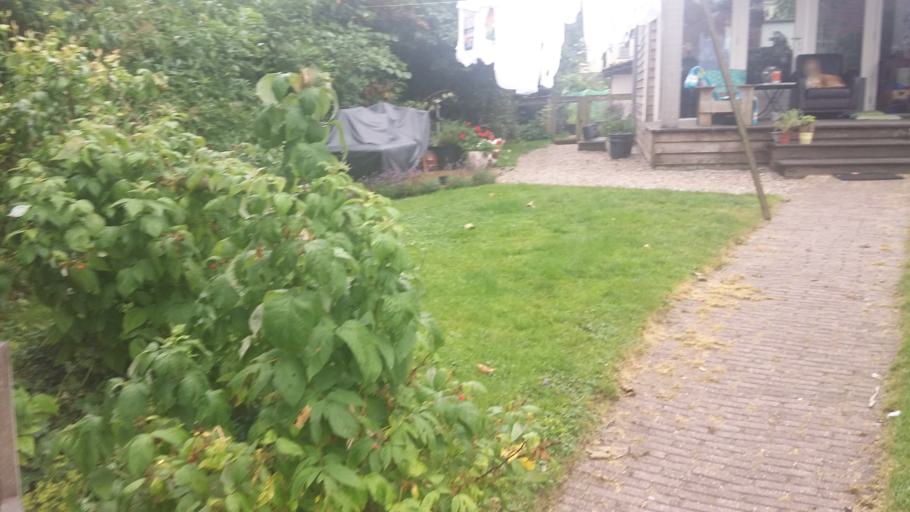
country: NL
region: Friesland
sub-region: Gemeente Littenseradiel
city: Mantgum
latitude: 53.1294
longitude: 5.7198
